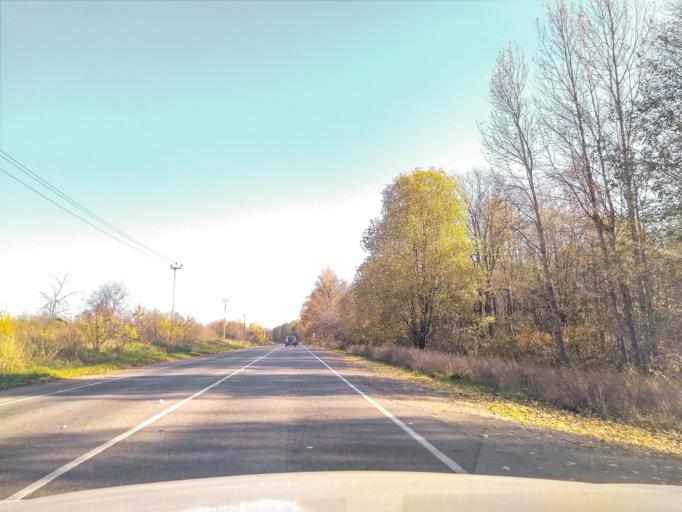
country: RU
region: Leningrad
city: Rozhdestveno
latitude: 59.3462
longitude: 29.9737
